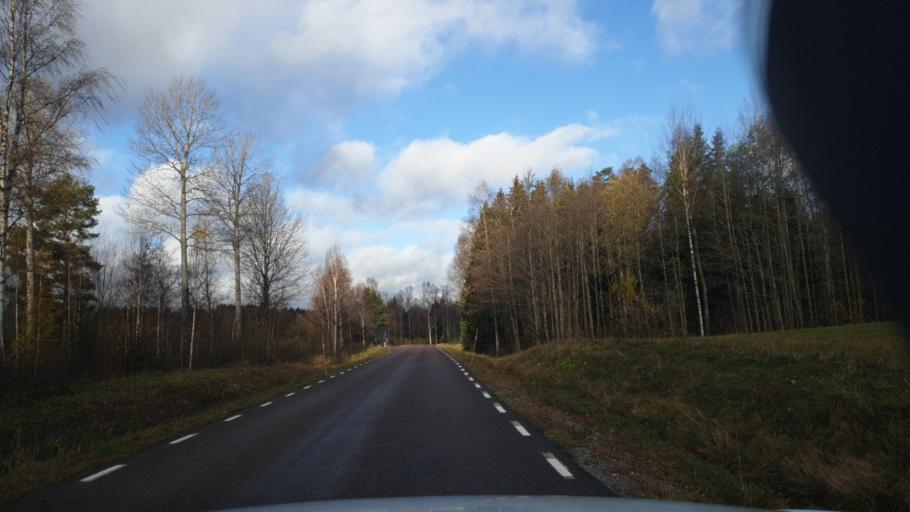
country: SE
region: Vaermland
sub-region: Grums Kommun
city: Slottsbron
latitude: 59.4792
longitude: 12.8848
